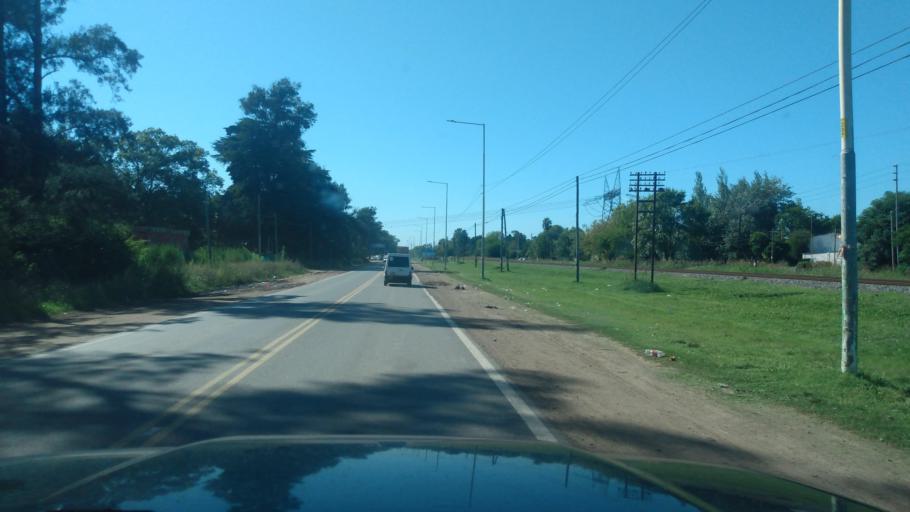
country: AR
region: Buenos Aires
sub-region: Partido de General Rodriguez
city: General Rodriguez
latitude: -34.6009
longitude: -58.9862
